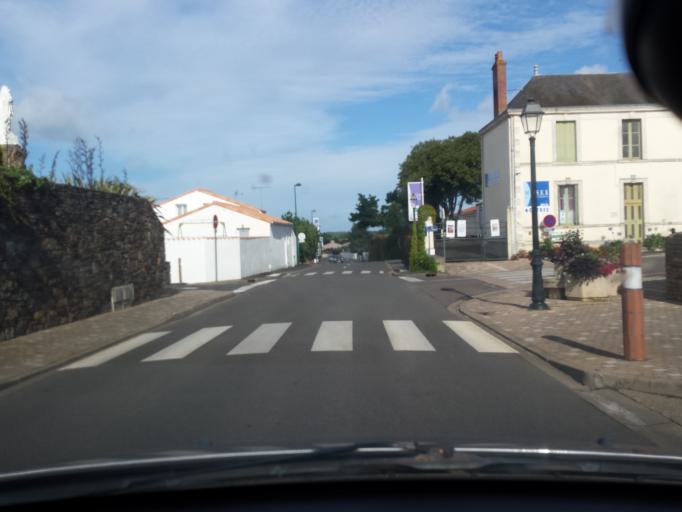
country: FR
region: Pays de la Loire
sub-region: Departement de la Vendee
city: Olonne-sur-Mer
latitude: 46.5374
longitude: -1.7762
